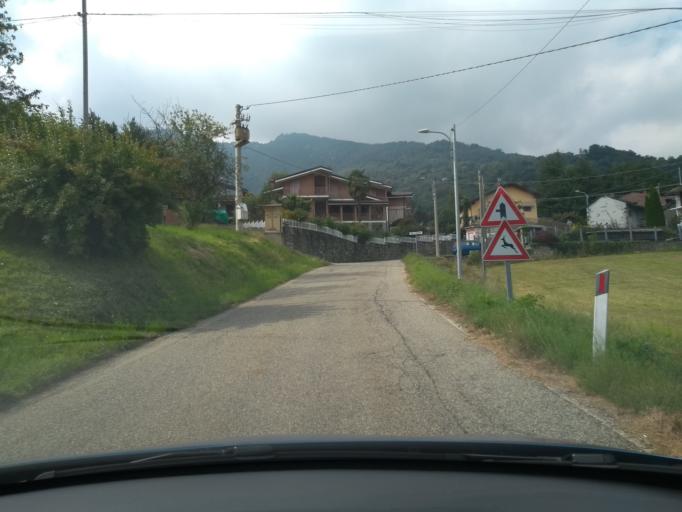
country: IT
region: Piedmont
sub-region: Provincia di Torino
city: Corio
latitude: 45.3168
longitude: 7.5215
